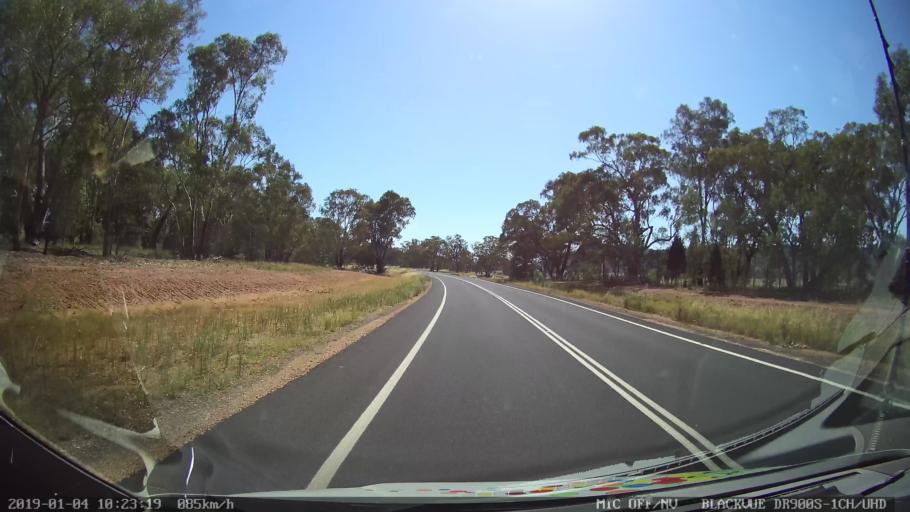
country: AU
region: New South Wales
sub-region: Cabonne
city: Canowindra
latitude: -33.3719
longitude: 148.5377
